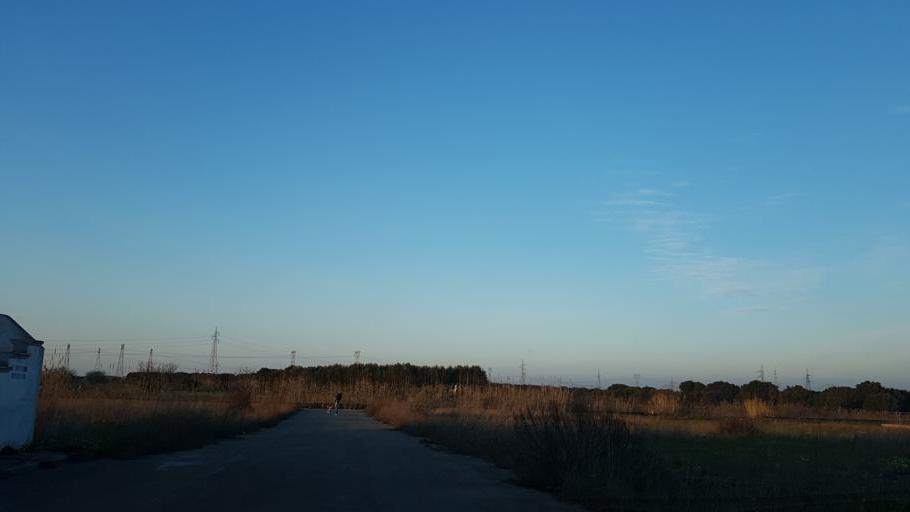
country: IT
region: Apulia
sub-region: Provincia di Brindisi
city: Tuturano
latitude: 40.5485
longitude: 17.9451
